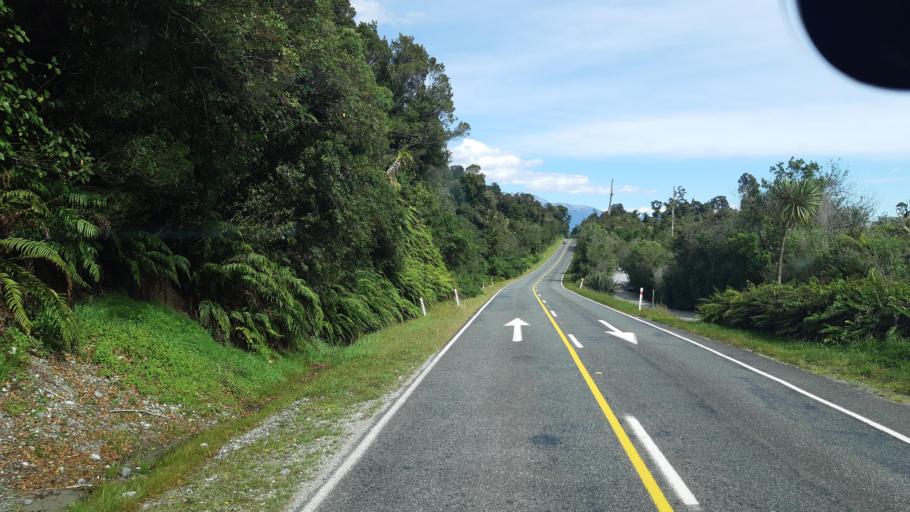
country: NZ
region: West Coast
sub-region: Westland District
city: Hokitika
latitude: -43.0586
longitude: 170.6353
